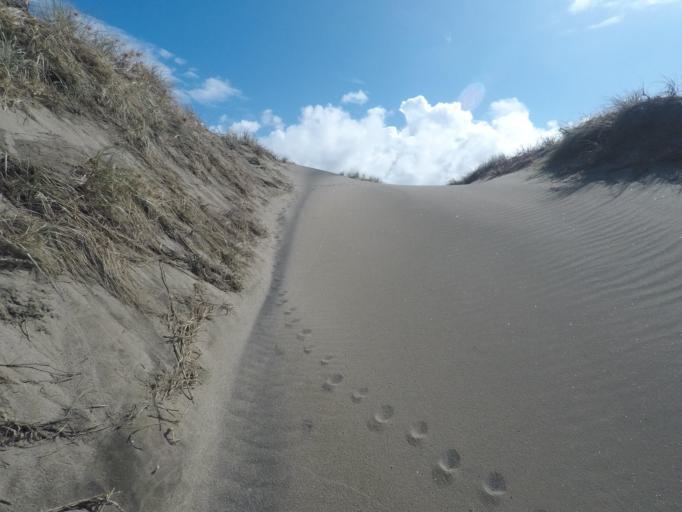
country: NZ
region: Auckland
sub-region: Auckland
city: Parakai
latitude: -36.6069
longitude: 174.2702
